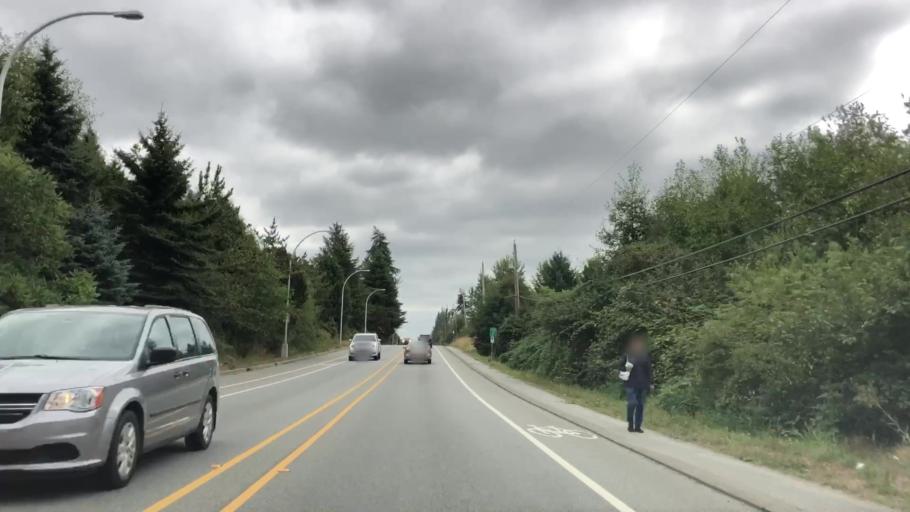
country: CA
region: British Columbia
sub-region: Greater Vancouver Regional District
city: White Rock
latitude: 49.0601
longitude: -122.7742
